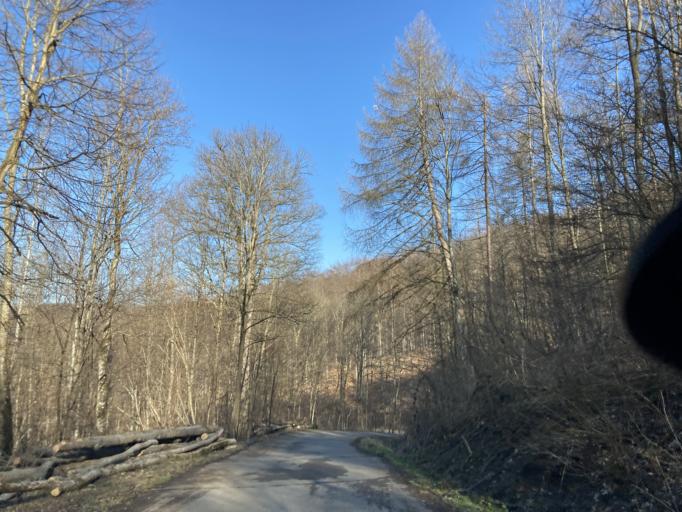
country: DE
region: Baden-Wuerttemberg
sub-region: Tuebingen Region
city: Mossingen
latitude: 48.3720
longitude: 9.0240
